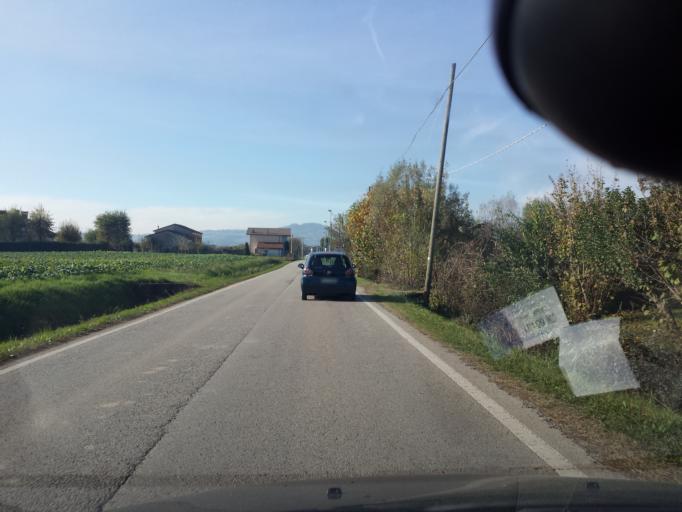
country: IT
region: Veneto
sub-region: Provincia di Vicenza
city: Dueville
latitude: 45.6102
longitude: 11.5372
